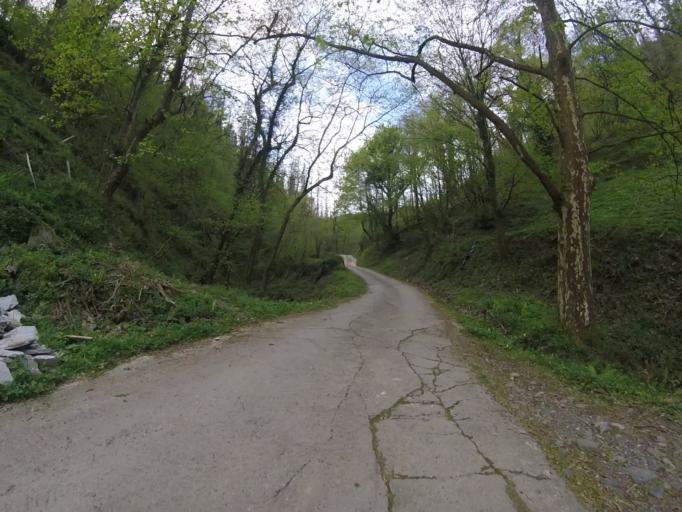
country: ES
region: Basque Country
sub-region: Provincia de Guipuzcoa
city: Errezil
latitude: 43.2065
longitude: -2.1817
